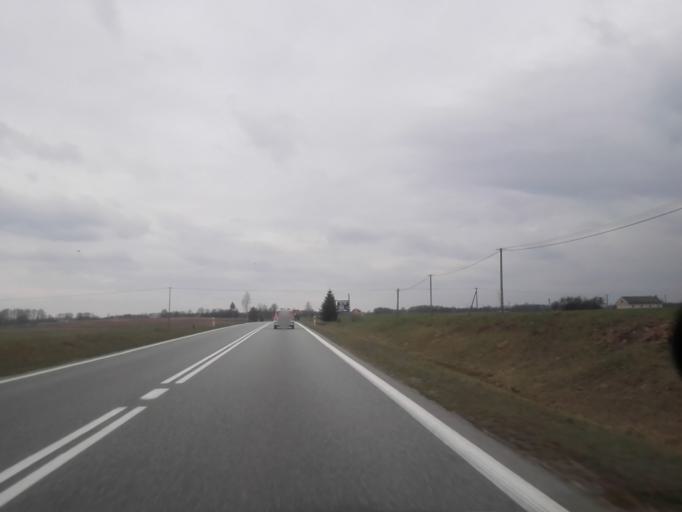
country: PL
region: Podlasie
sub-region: Powiat augustowski
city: Augustow
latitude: 53.8128
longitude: 22.9155
